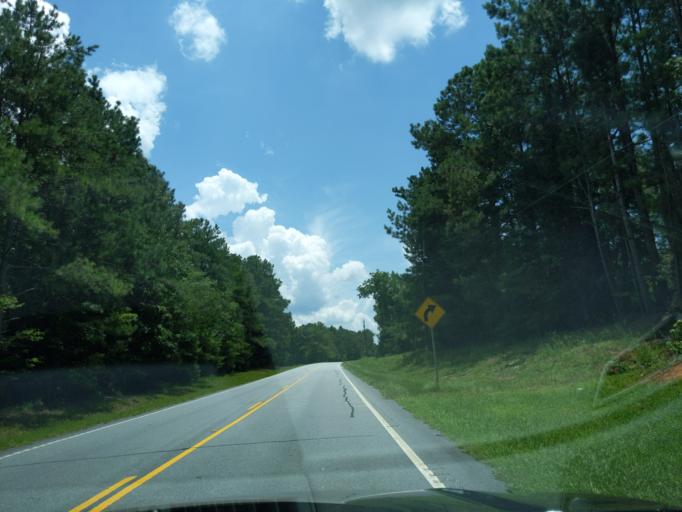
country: US
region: South Carolina
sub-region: Greenwood County
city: Ninety Six
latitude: 33.9862
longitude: -82.0456
